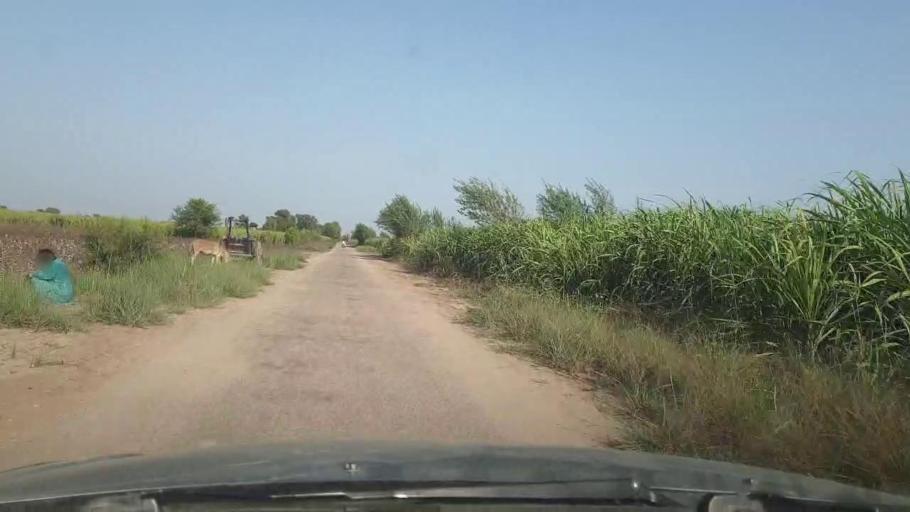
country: PK
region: Sindh
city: Tando Ghulam Ali
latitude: 25.2095
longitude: 68.9572
